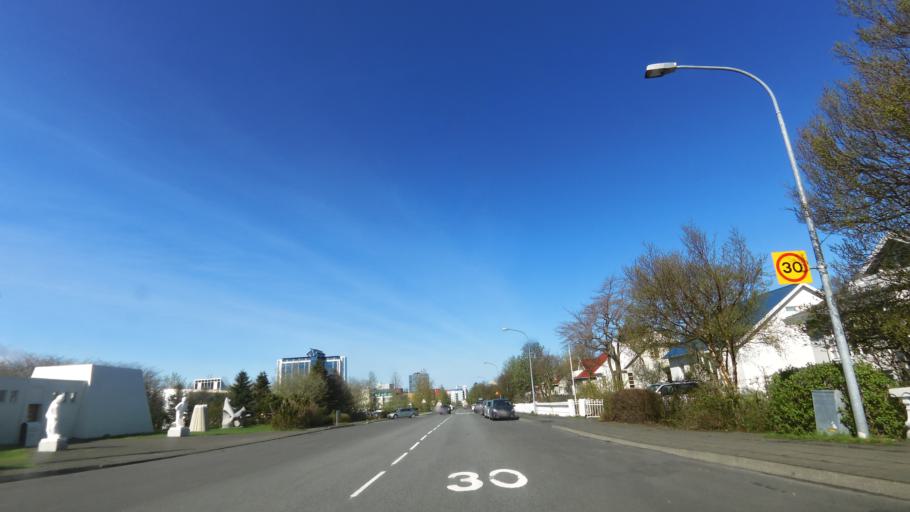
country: IS
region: Capital Region
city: Reykjavik
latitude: 64.1417
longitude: -21.8842
